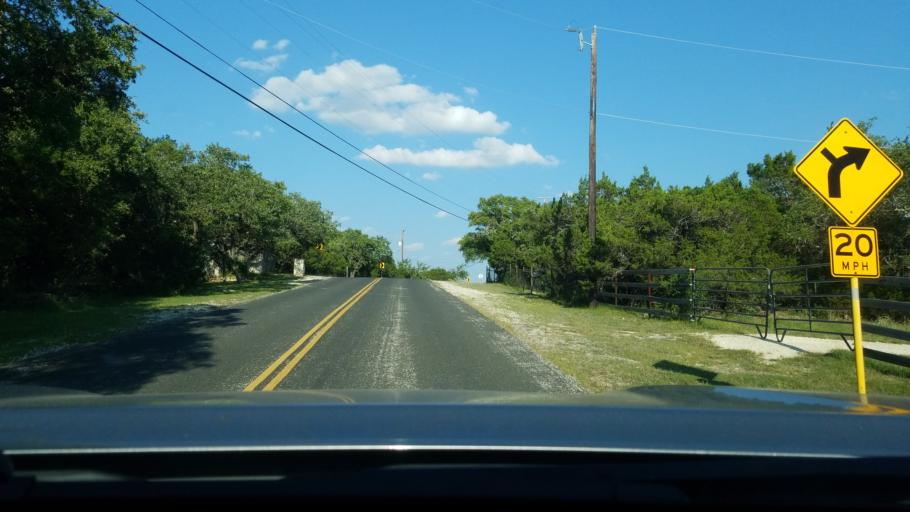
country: US
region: Texas
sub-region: Comal County
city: Bulverde
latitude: 29.7134
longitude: -98.4380
